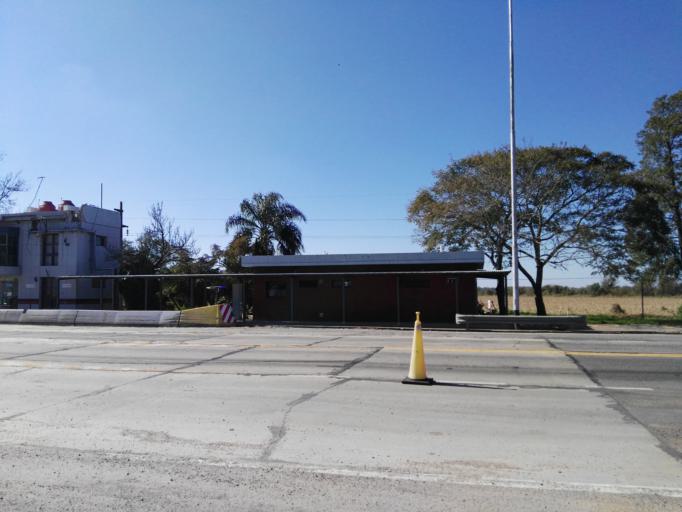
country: AR
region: Santa Fe
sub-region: Departamento de General Obligado
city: Reconquista
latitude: -29.2262
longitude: -59.7195
